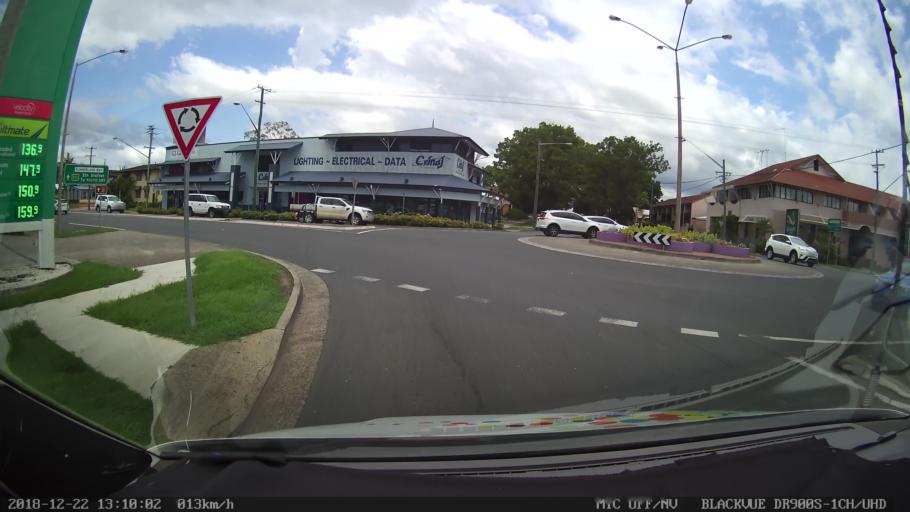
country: AU
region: New South Wales
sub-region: Clarence Valley
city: Grafton
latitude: -29.6931
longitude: 152.9372
